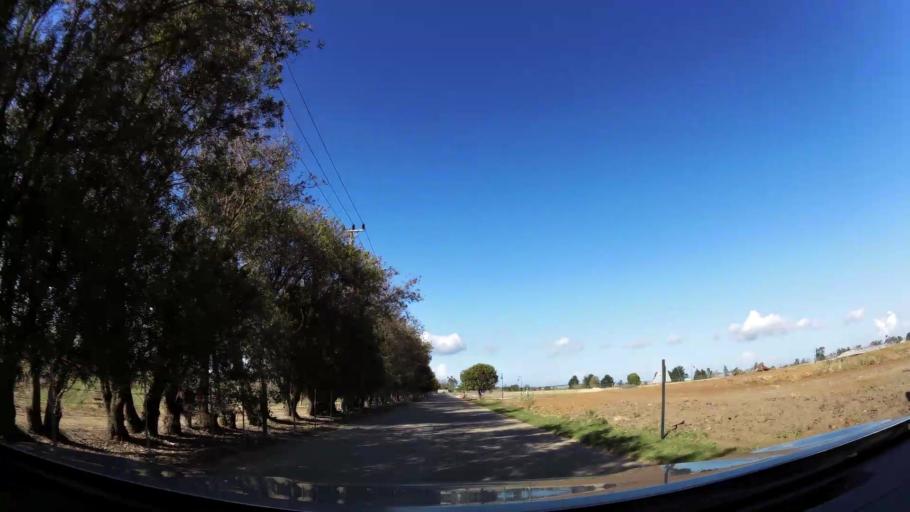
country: ZA
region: Western Cape
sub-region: Eden District Municipality
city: George
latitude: -33.9586
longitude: 22.3987
